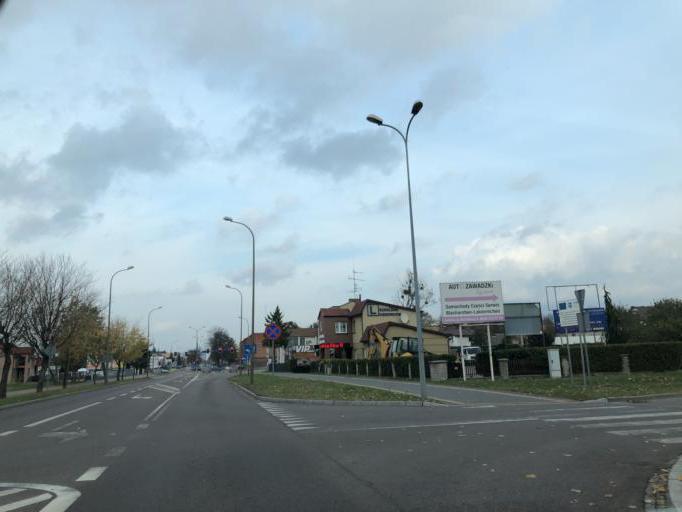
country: PL
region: Podlasie
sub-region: Lomza
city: Lomza
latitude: 53.1602
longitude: 22.0561
